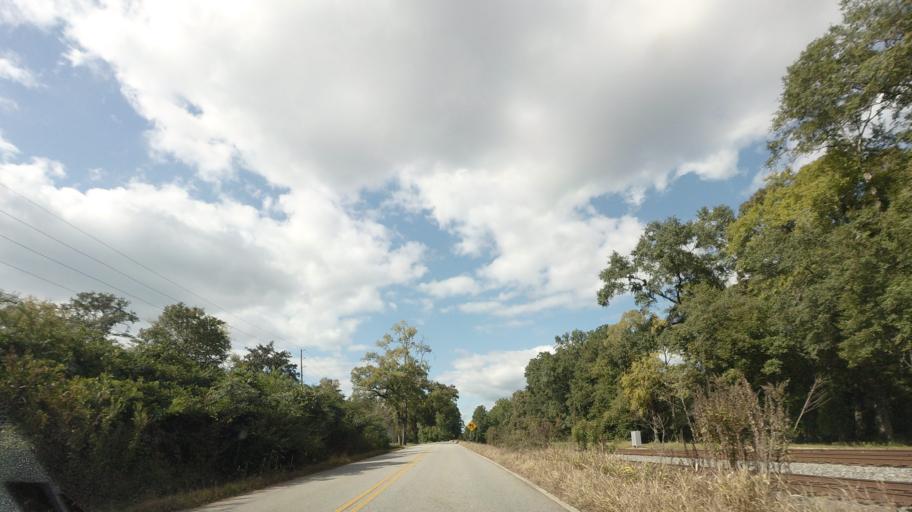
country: US
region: Georgia
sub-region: Bibb County
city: Macon
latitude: 32.9320
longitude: -83.7024
